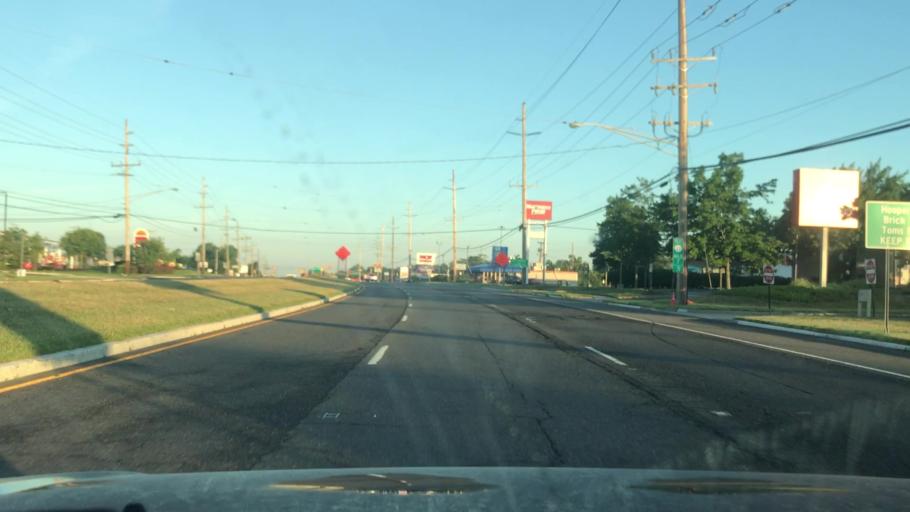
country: US
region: New Jersey
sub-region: Ocean County
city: Toms River
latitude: 39.9631
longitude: -74.1839
